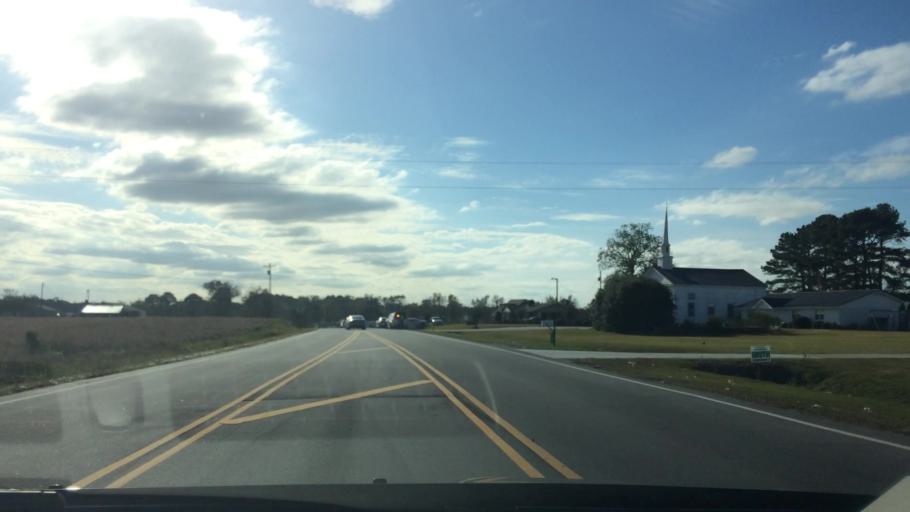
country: US
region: North Carolina
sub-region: Greene County
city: Snow Hill
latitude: 35.4468
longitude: -77.7400
